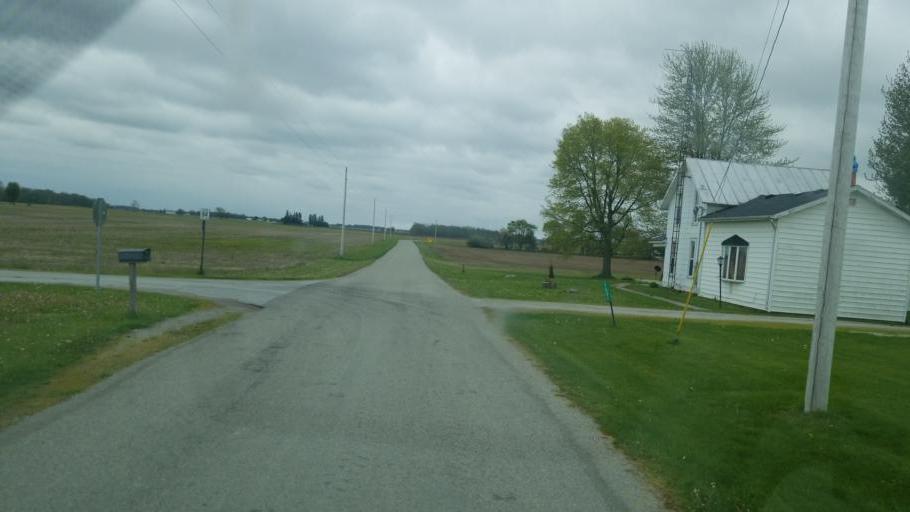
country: US
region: Ohio
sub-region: Hardin County
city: Kenton
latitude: 40.7106
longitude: -83.5950
